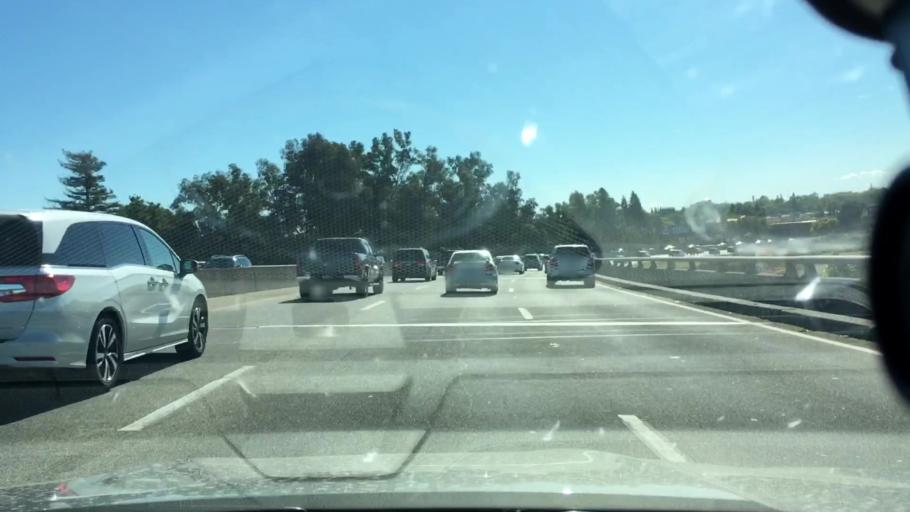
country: US
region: California
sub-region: Sacramento County
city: Sacramento
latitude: 38.5871
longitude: -121.4469
